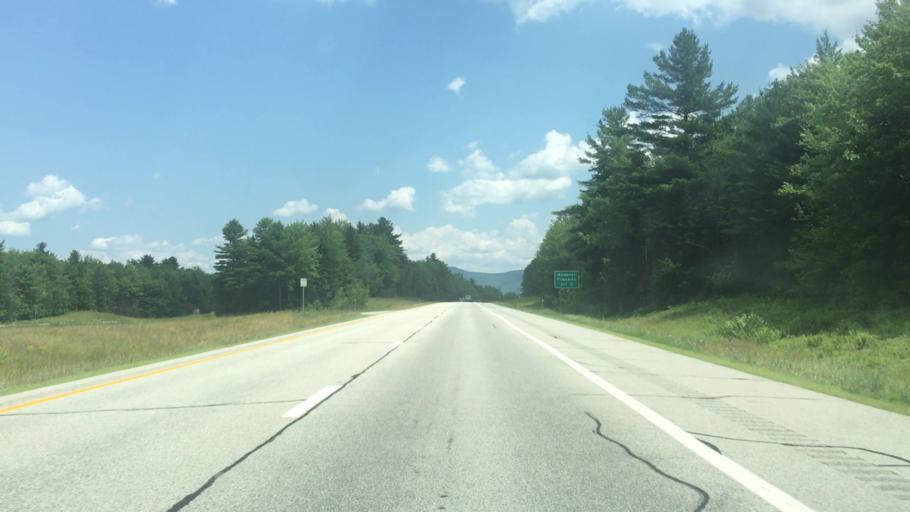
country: US
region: New Hampshire
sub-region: Merrimack County
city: New London
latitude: 43.3944
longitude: -71.9951
